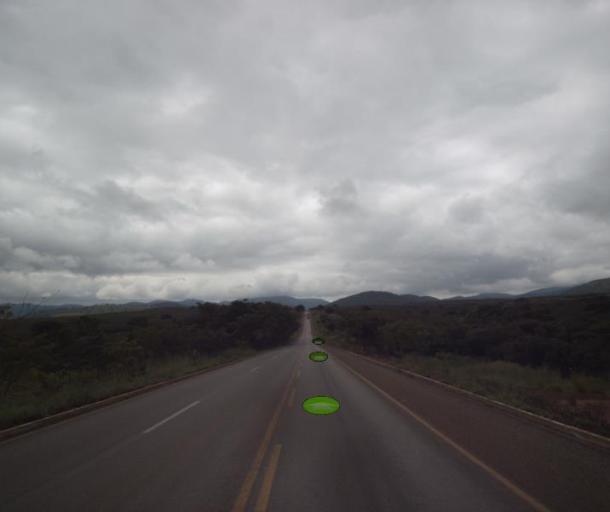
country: BR
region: Goias
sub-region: Barro Alto
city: Barro Alto
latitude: -14.8706
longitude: -49.0057
